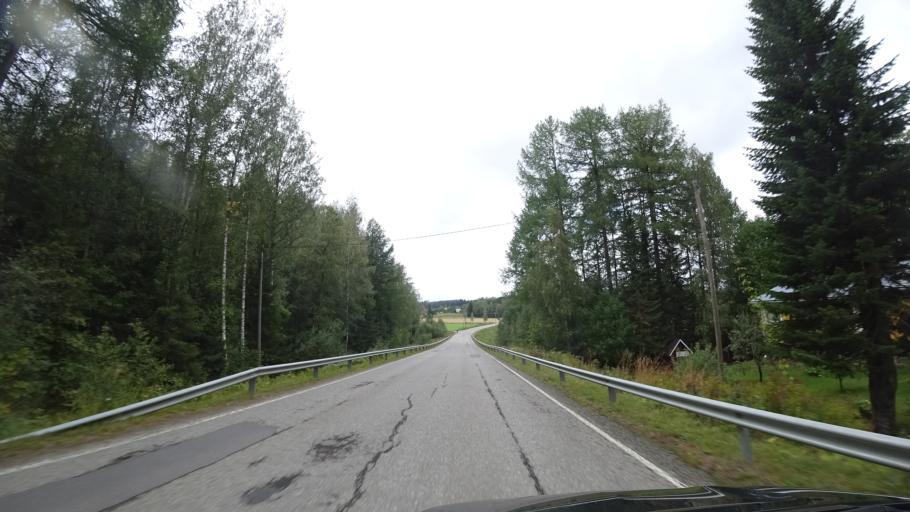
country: FI
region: Haeme
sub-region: Haemeenlinna
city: Lammi
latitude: 61.0423
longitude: 25.0152
